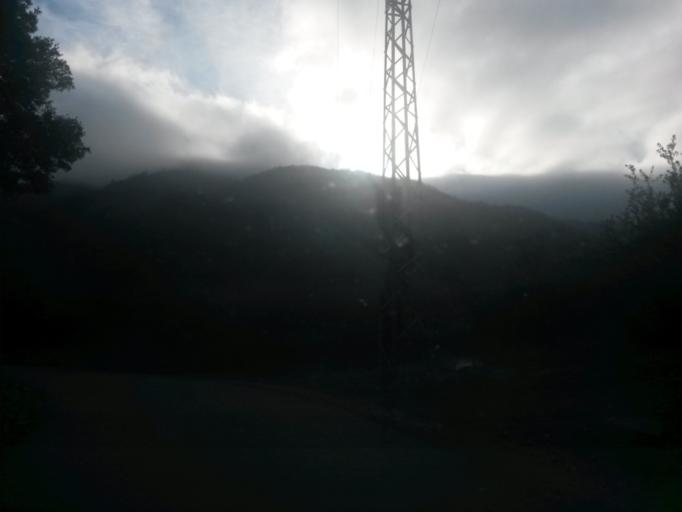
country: ES
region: Catalonia
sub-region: Provincia de Girona
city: Susqueda
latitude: 41.9739
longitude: 2.5224
